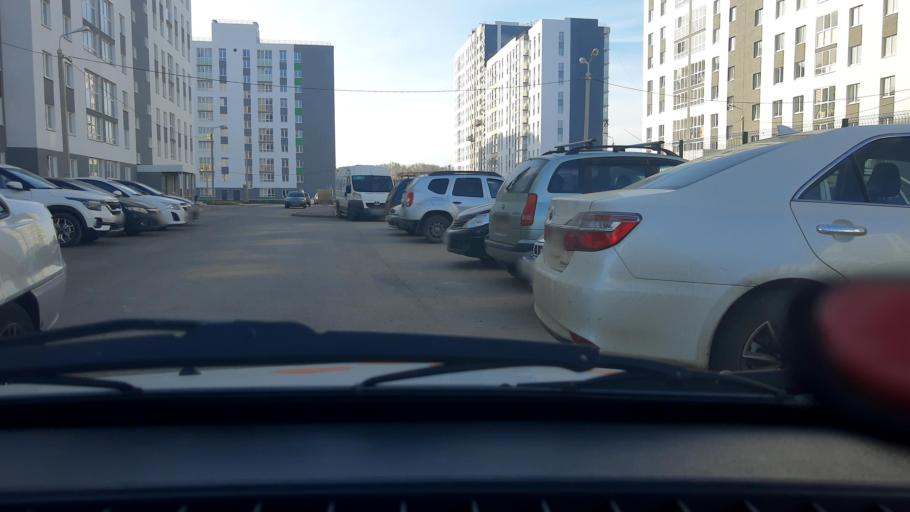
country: RU
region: Bashkortostan
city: Ufa
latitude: 54.6917
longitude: 55.9685
